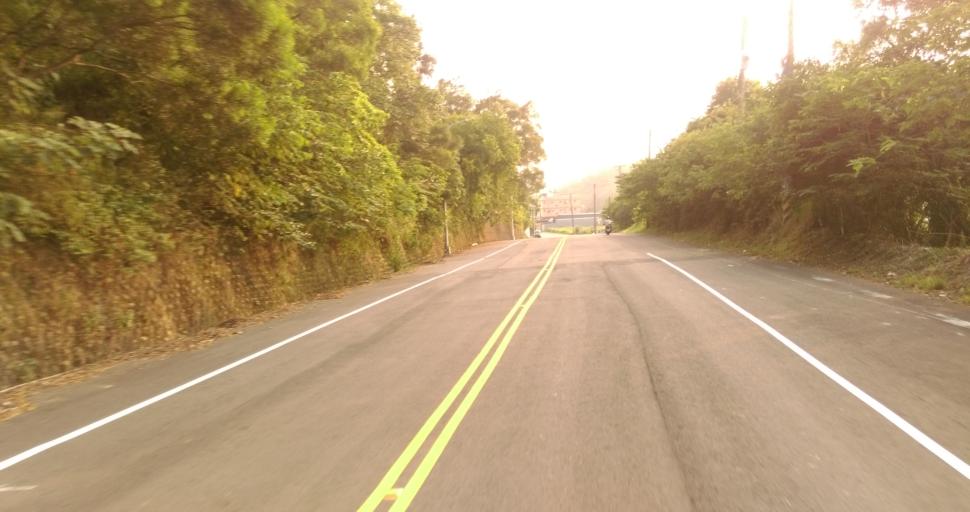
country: TW
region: Taiwan
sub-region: Hsinchu
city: Hsinchu
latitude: 24.7528
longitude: 120.9389
